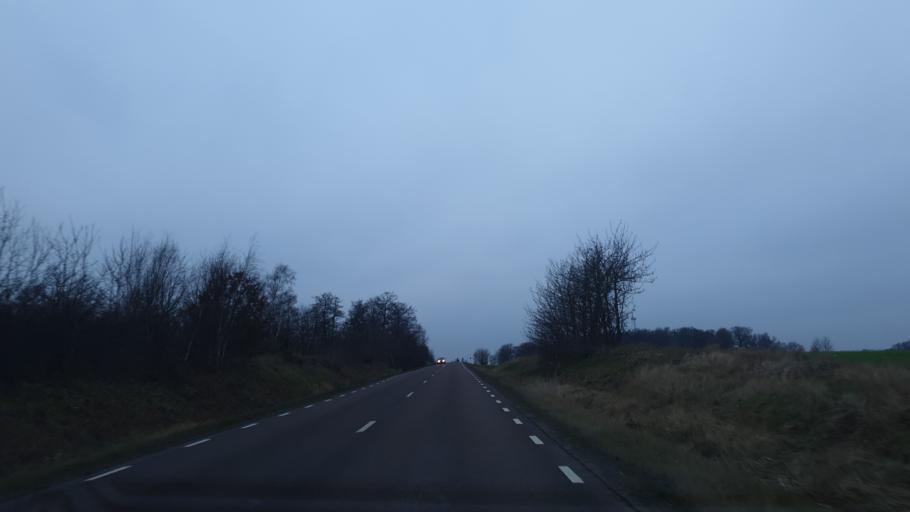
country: SE
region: Blekinge
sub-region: Karlskrona Kommun
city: Jaemjoe
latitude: 56.1634
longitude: 15.7623
